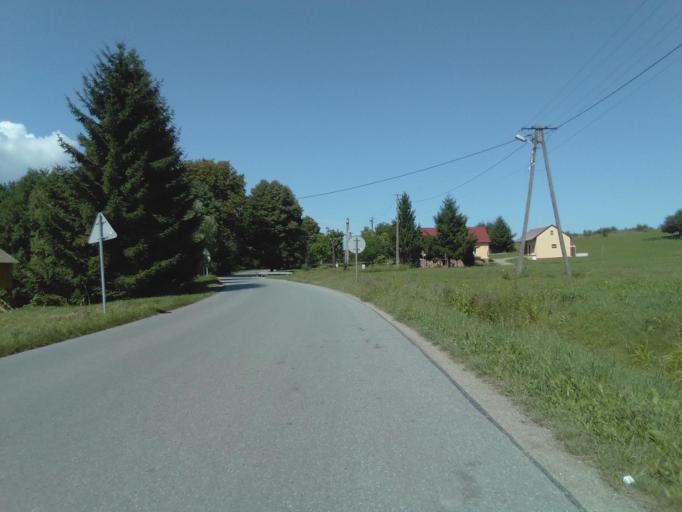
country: PL
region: Subcarpathian Voivodeship
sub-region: Powiat jasielski
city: Nowy Zmigrod
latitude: 49.6162
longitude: 21.5799
